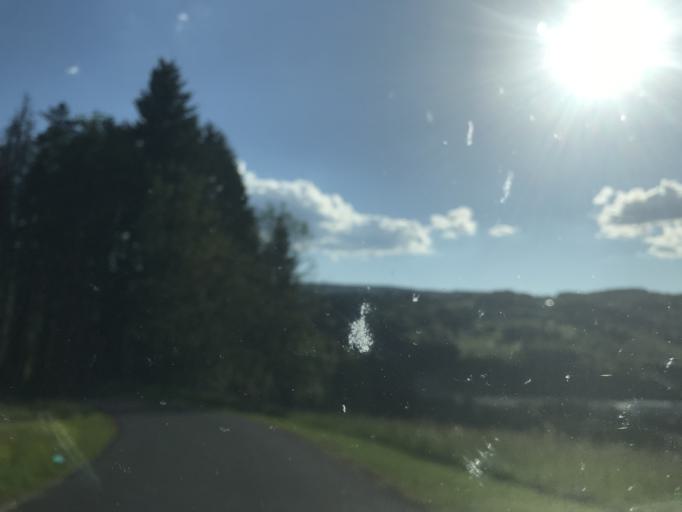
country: FR
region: Auvergne
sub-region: Departement du Puy-de-Dome
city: Job
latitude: 45.6383
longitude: 3.6725
